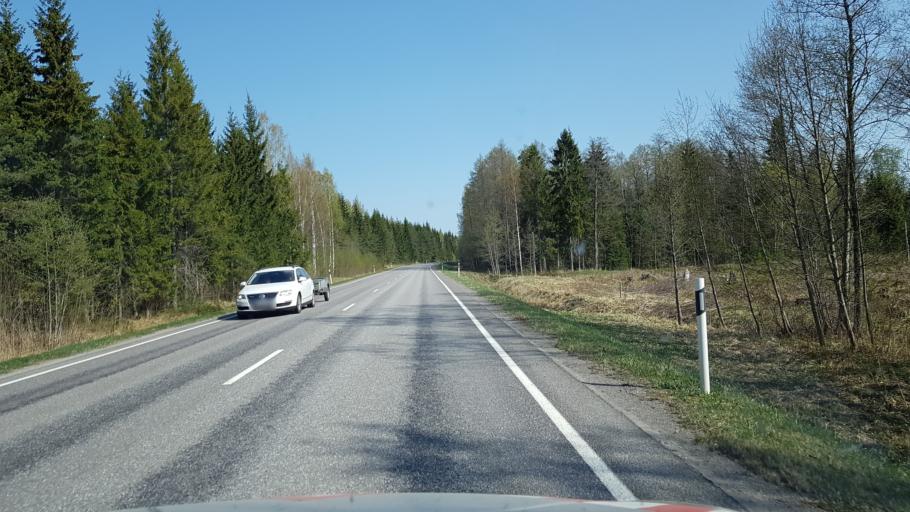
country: EE
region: Viljandimaa
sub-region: Moisakuela linn
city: Moisakula
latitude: 58.2330
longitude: 25.1176
